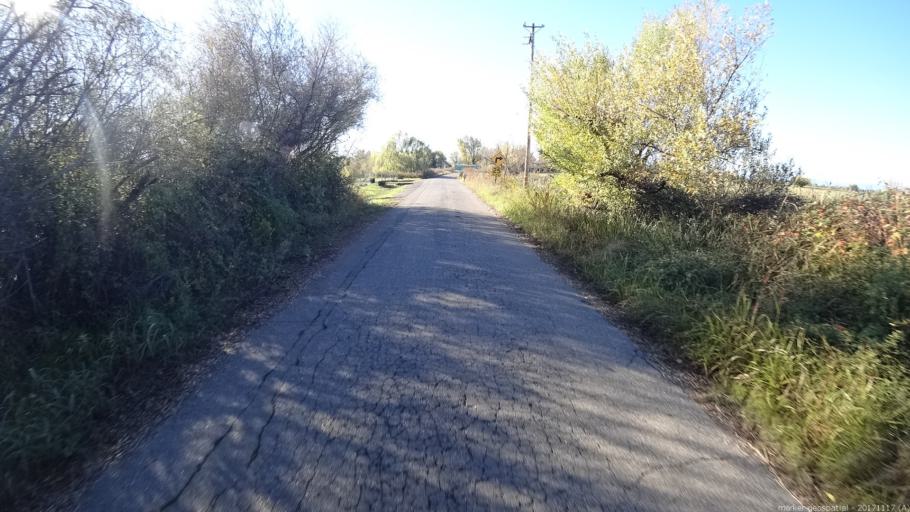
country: US
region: California
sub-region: Shasta County
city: Cottonwood
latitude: 40.3975
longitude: -122.2067
